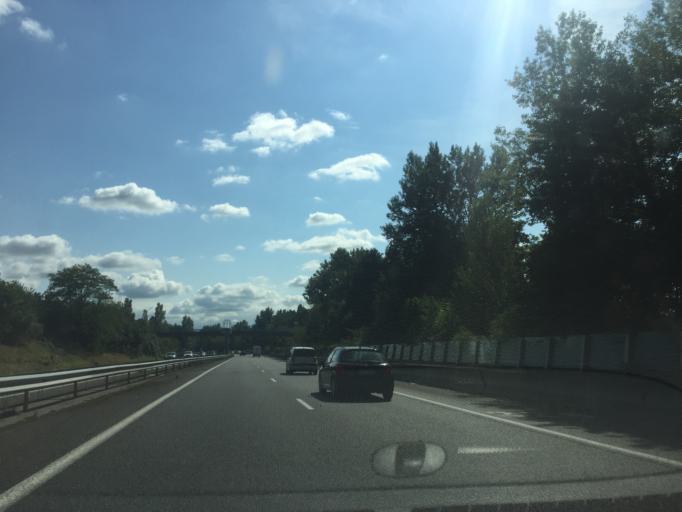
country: FR
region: Midi-Pyrenees
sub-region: Departement de la Haute-Garonne
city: Martres-Tolosane
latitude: 43.1746
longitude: 0.9766
